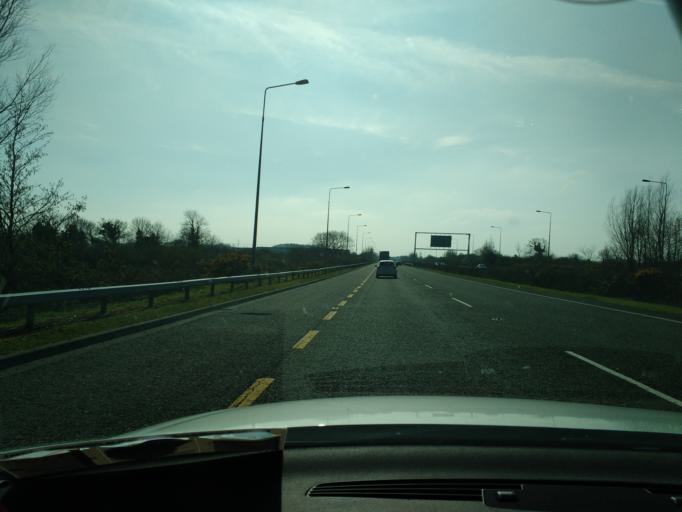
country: IE
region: Munster
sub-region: An Clar
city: Shannon
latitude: 52.7227
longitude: -8.8773
